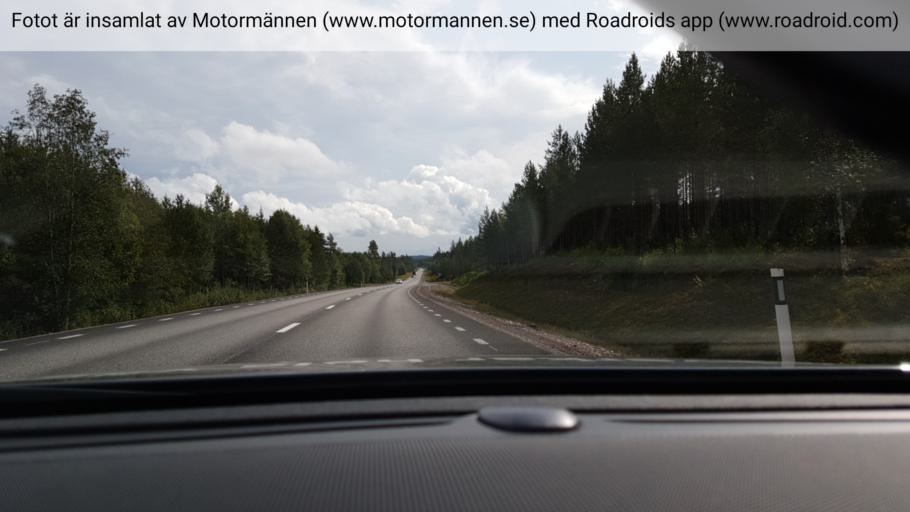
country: SE
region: Dalarna
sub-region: Rattviks Kommun
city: Raettvik
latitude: 60.8189
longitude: 15.2578
